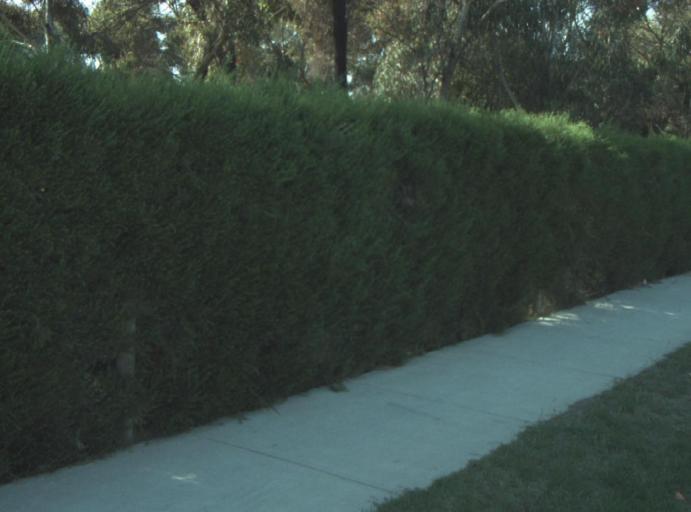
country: AU
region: Victoria
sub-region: Greater Geelong
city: Leopold
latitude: -38.1895
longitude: 144.4550
